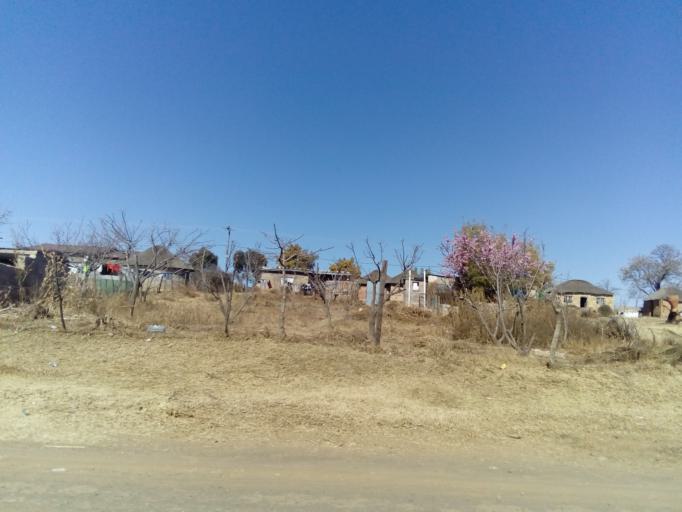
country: LS
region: Berea
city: Teyateyaneng
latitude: -29.1238
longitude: 27.8282
